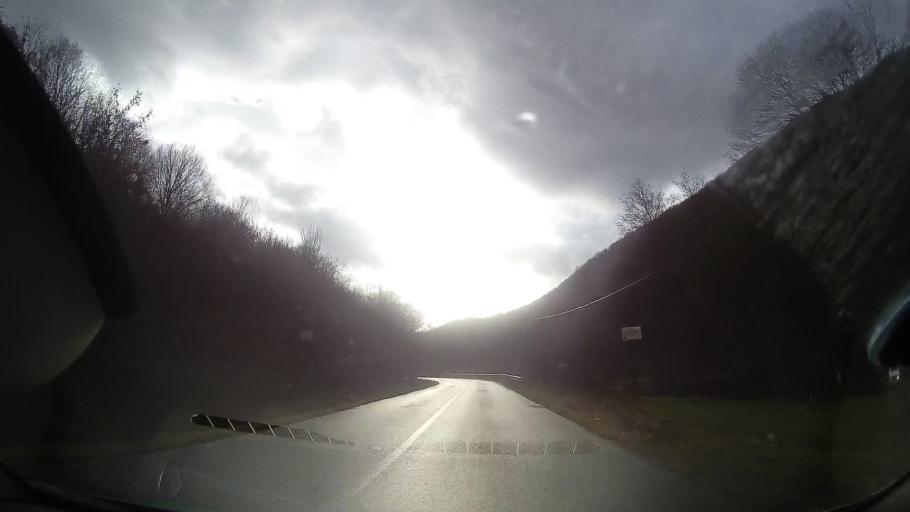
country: RO
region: Alba
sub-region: Comuna Rimetea
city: Rimetea
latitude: 46.4932
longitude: 23.5796
